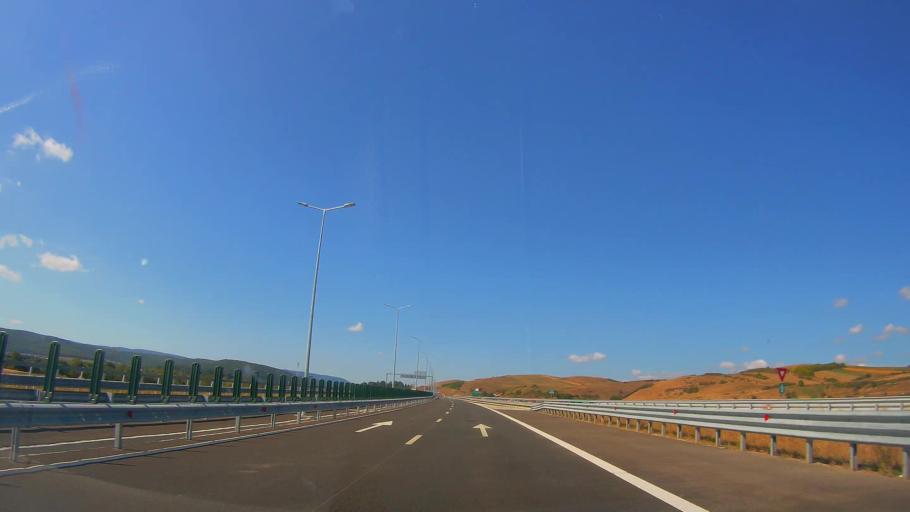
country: RO
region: Cluj
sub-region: Comuna Floresti
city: Luna de Sus
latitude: 46.7573
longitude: 23.4079
